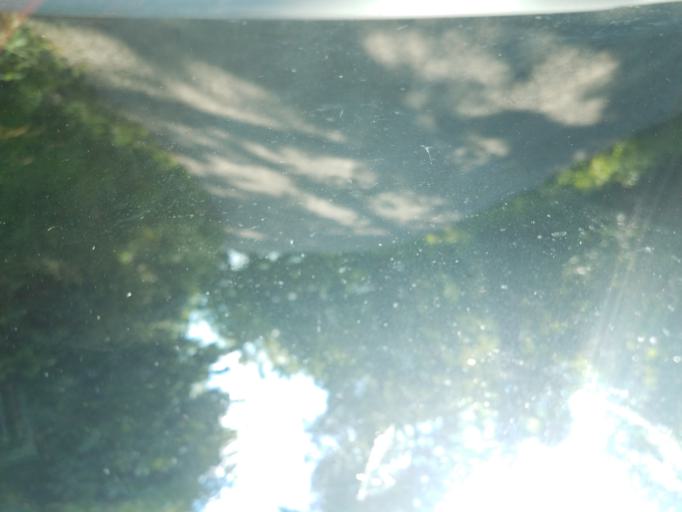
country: US
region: Ohio
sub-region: Gallia County
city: Gallipolis
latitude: 38.7432
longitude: -82.3473
